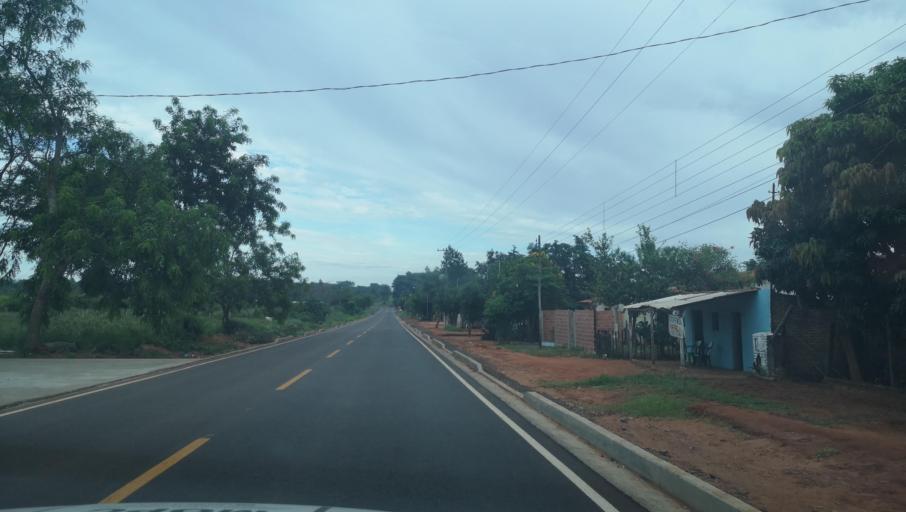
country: PY
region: San Pedro
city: Capiibary
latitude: -24.7440
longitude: -56.0316
